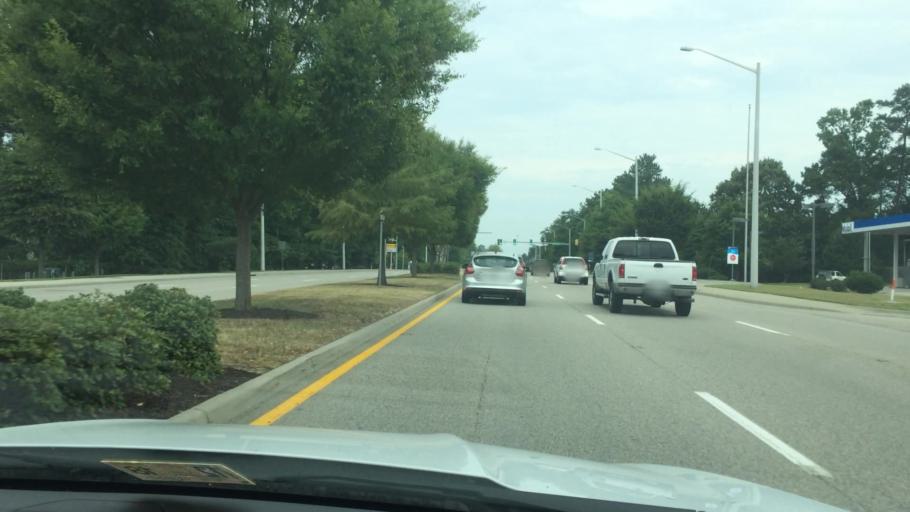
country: US
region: Virginia
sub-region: York County
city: Yorktown
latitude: 37.1542
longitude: -76.5322
